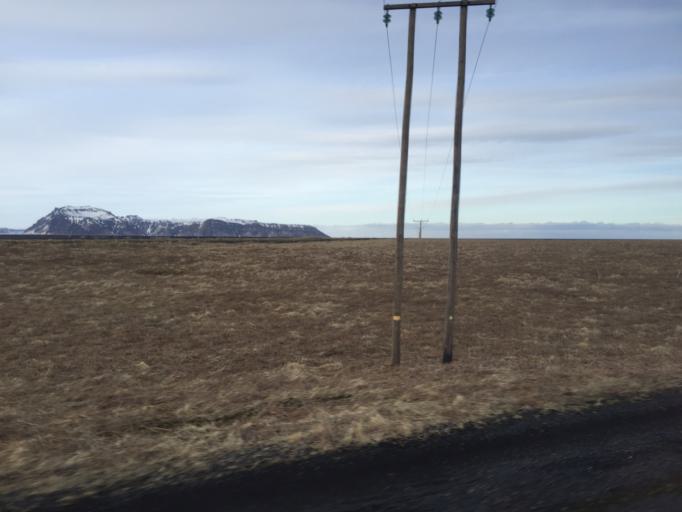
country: IS
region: South
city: Vestmannaeyjar
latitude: 63.4371
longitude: -18.8182
